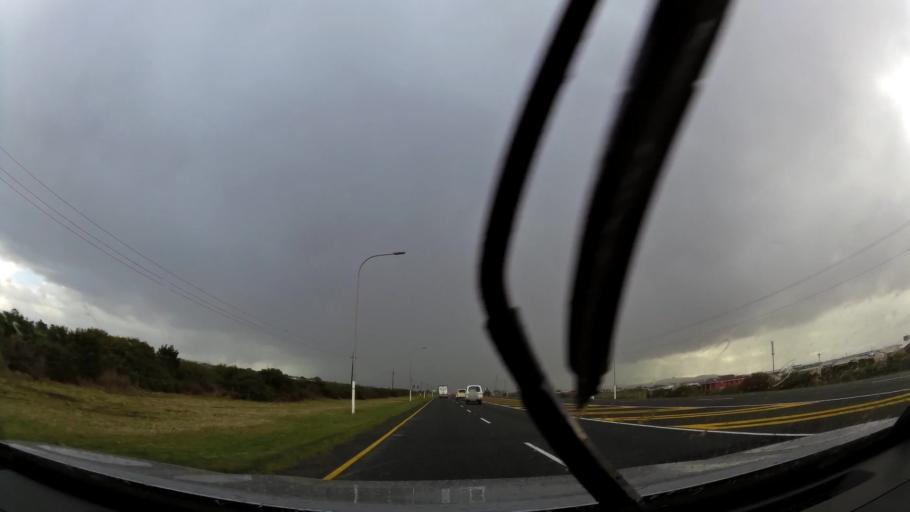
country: ZA
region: Western Cape
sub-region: Eden District Municipality
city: Mossel Bay
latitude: -34.1828
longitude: 22.0935
